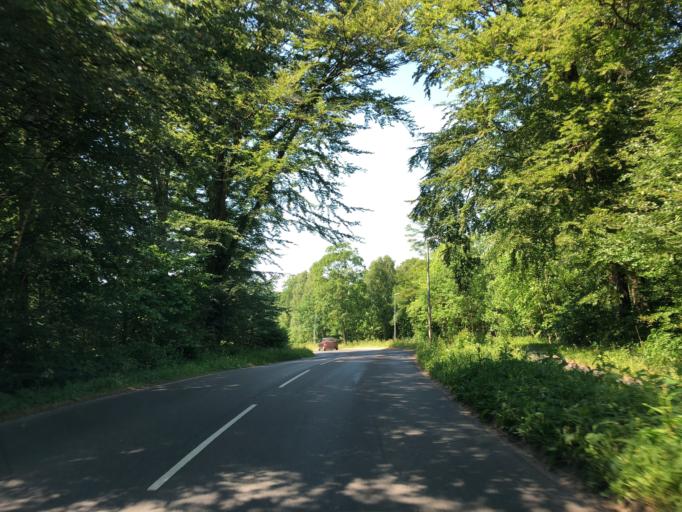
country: DK
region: South Denmark
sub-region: Kolding Kommune
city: Kolding
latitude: 55.5115
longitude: 9.4931
